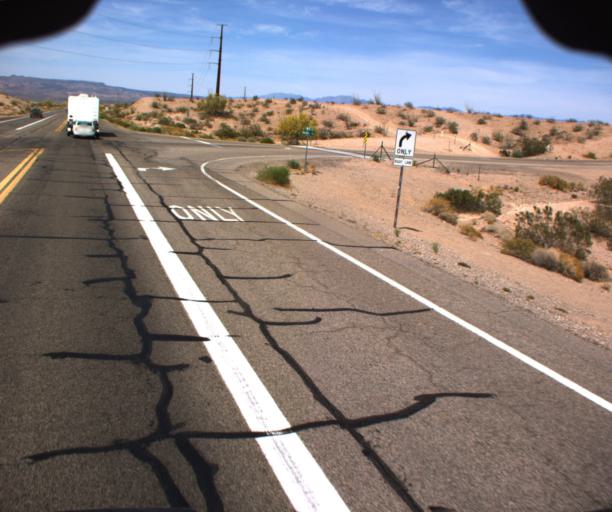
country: US
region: Arizona
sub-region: Mohave County
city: Desert Hills
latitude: 34.6622
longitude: -114.3144
